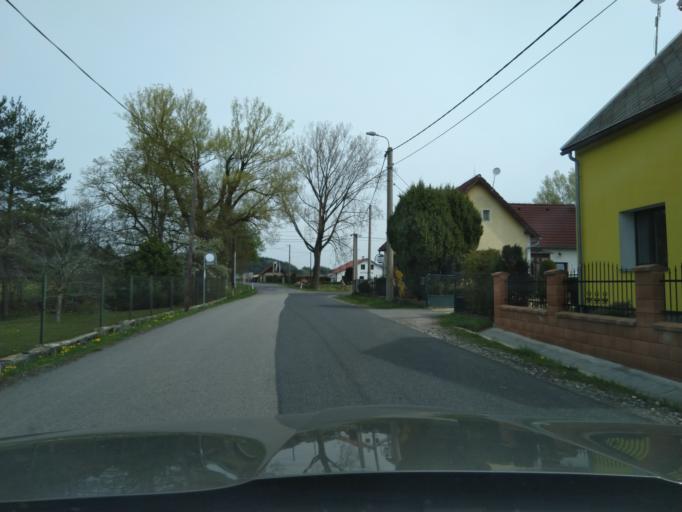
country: CZ
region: Jihocesky
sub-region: Okres Prachatice
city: Stachy
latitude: 49.1839
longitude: 13.6456
